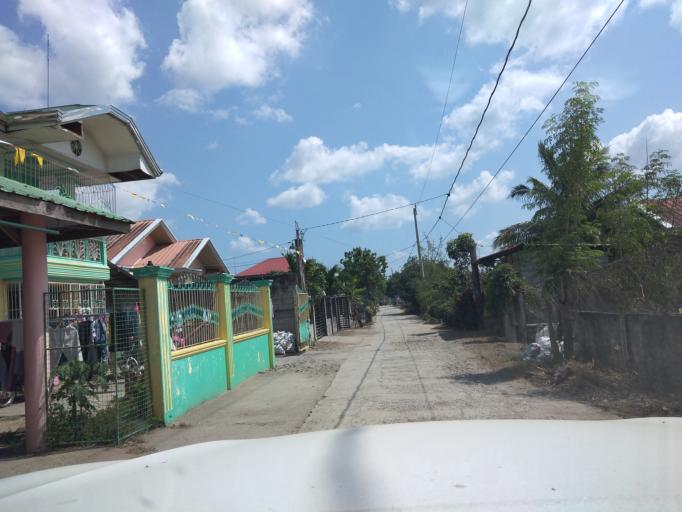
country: PH
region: Central Luzon
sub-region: Province of Pampanga
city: Bahay Pare
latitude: 15.0441
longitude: 120.8847
